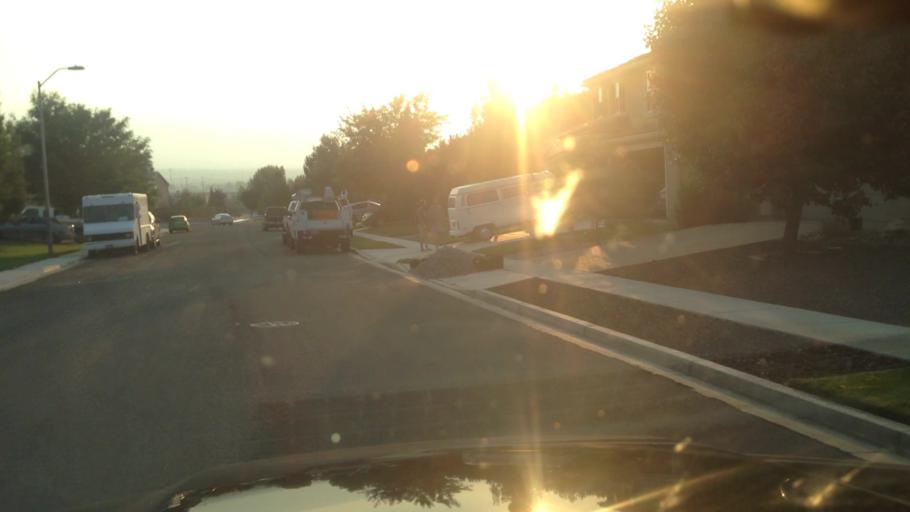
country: US
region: Nevada
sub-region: Washoe County
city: Sparks
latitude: 39.4109
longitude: -119.7385
